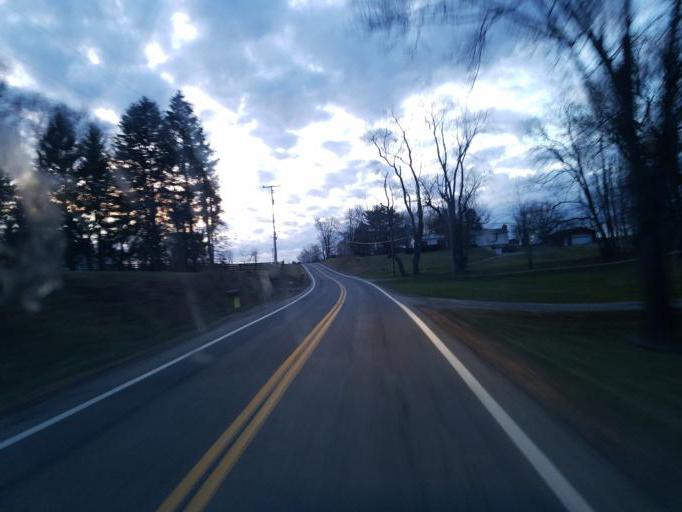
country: US
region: Ohio
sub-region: Knox County
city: Gambier
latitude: 40.2805
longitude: -82.3115
